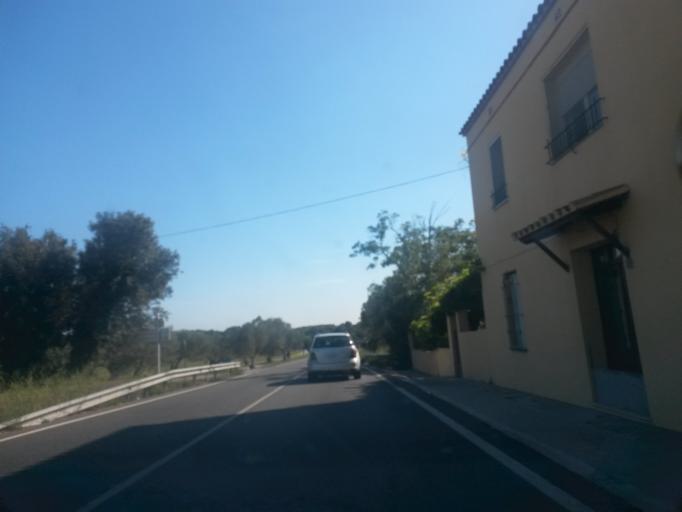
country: ES
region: Catalonia
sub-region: Provincia de Girona
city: Regencos
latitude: 41.9497
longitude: 3.1664
